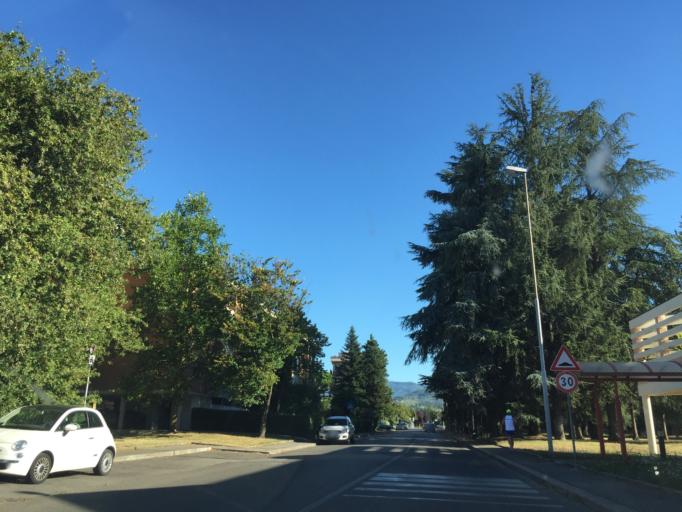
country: IT
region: Tuscany
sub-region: Provincia di Pistoia
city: Pistoia
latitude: 43.9368
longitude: 10.8976
